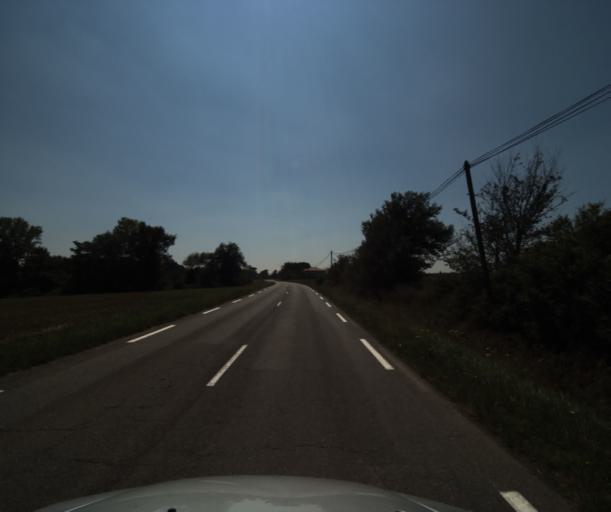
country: FR
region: Midi-Pyrenees
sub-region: Departement de la Haute-Garonne
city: Seysses
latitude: 43.4571
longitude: 1.2909
